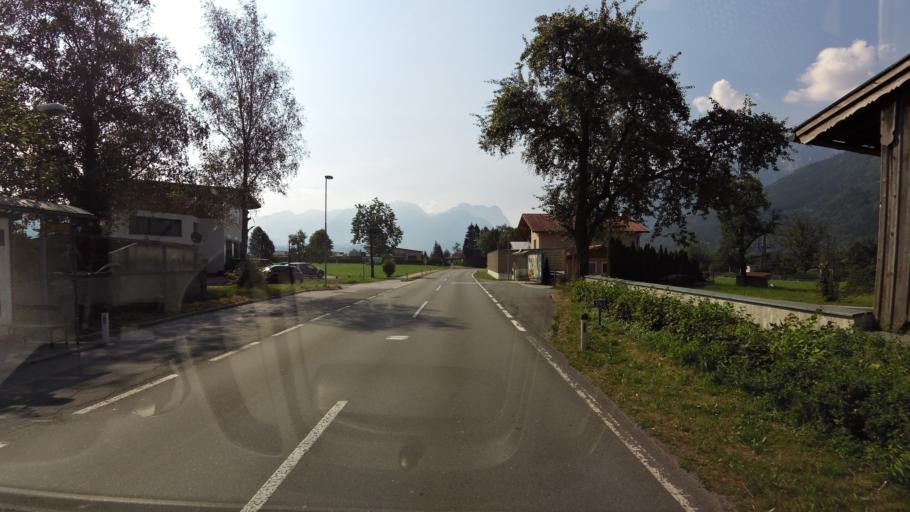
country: AT
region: Salzburg
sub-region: Politischer Bezirk Hallein
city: Kuchl
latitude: 47.6446
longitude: 13.1339
